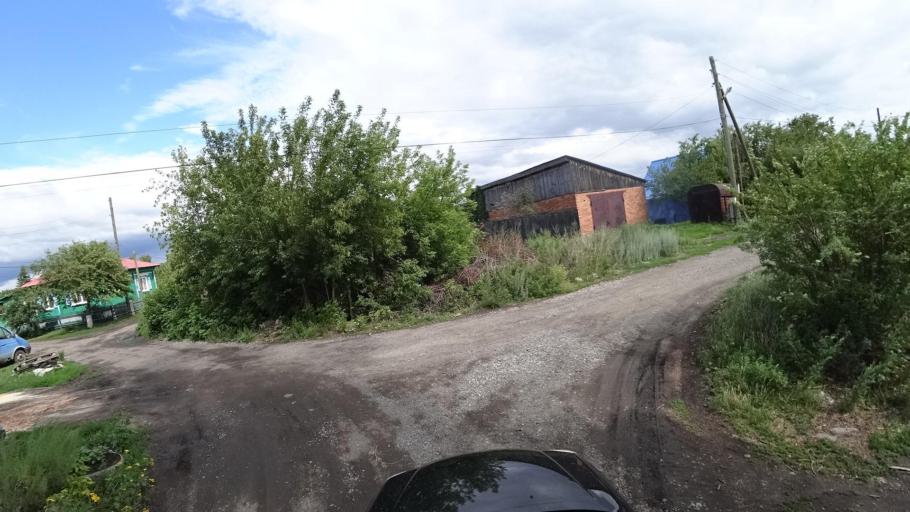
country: RU
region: Sverdlovsk
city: Kamyshlov
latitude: 56.8589
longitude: 62.7106
